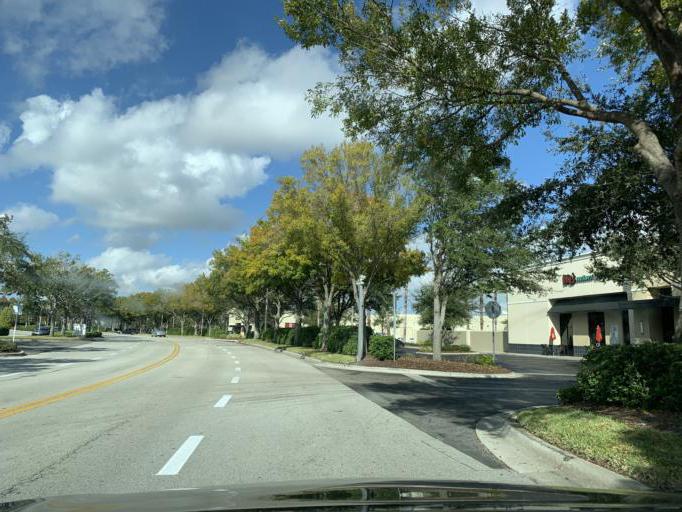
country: US
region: Florida
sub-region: Orange County
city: Oak Ridge
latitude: 28.4875
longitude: -81.4298
